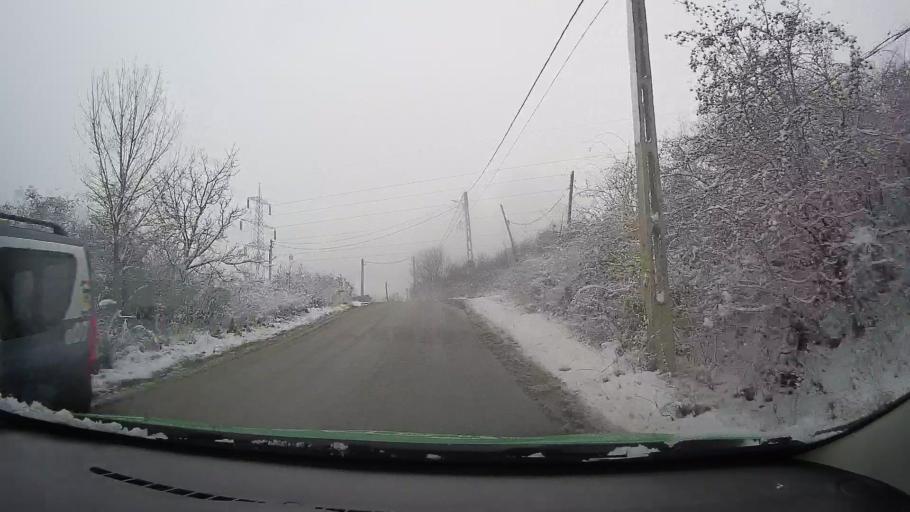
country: RO
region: Hunedoara
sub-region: Municipiul Deva
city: Deva
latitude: 45.8678
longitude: 22.8910
